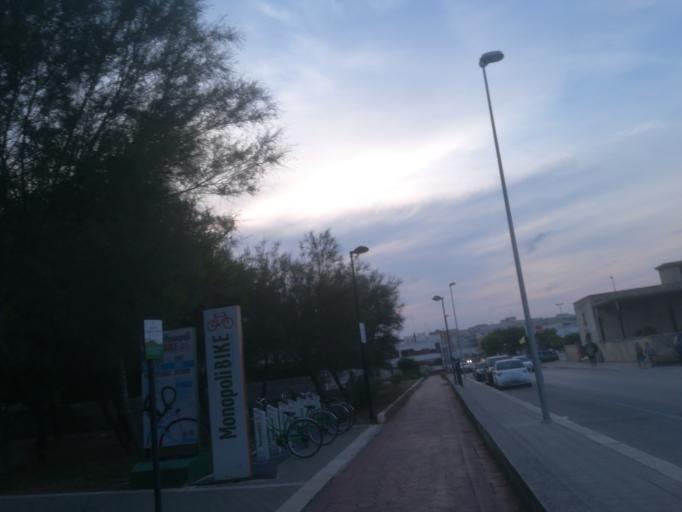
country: IT
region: Apulia
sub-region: Provincia di Bari
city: Monopoli
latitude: 40.9453
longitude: 17.3091
